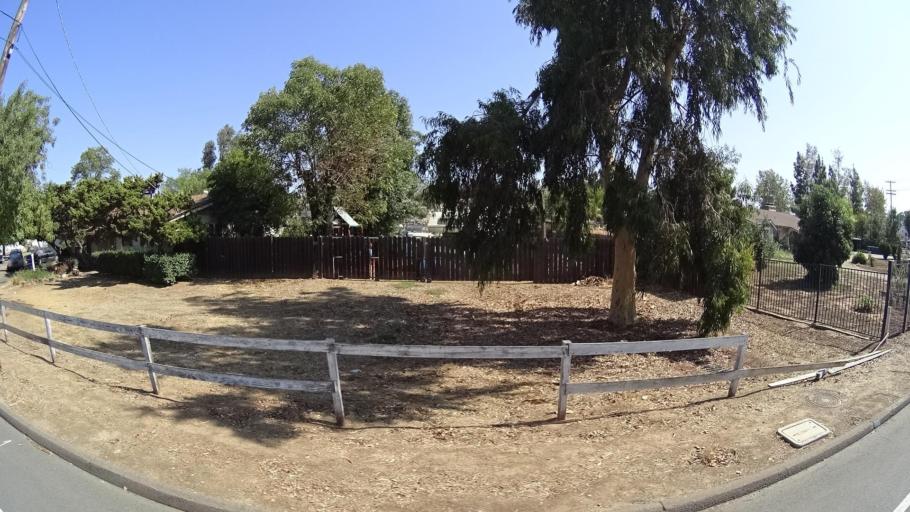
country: US
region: California
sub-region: San Diego County
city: Granite Hills
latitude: 32.7958
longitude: -116.9214
